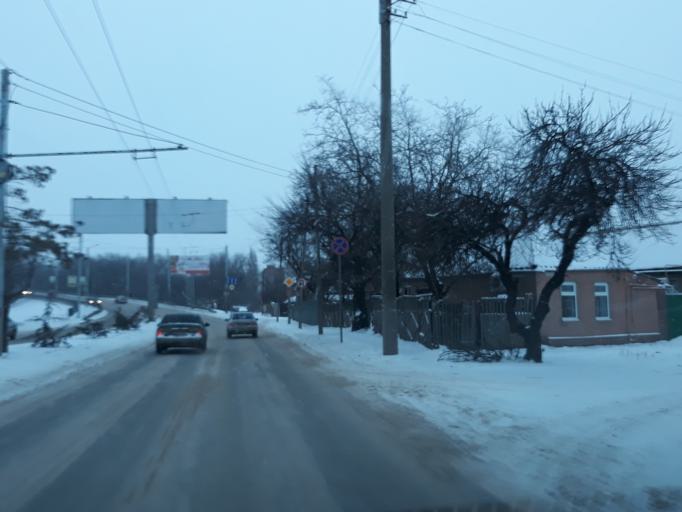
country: RU
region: Rostov
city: Taganrog
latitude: 47.2622
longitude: 38.9261
